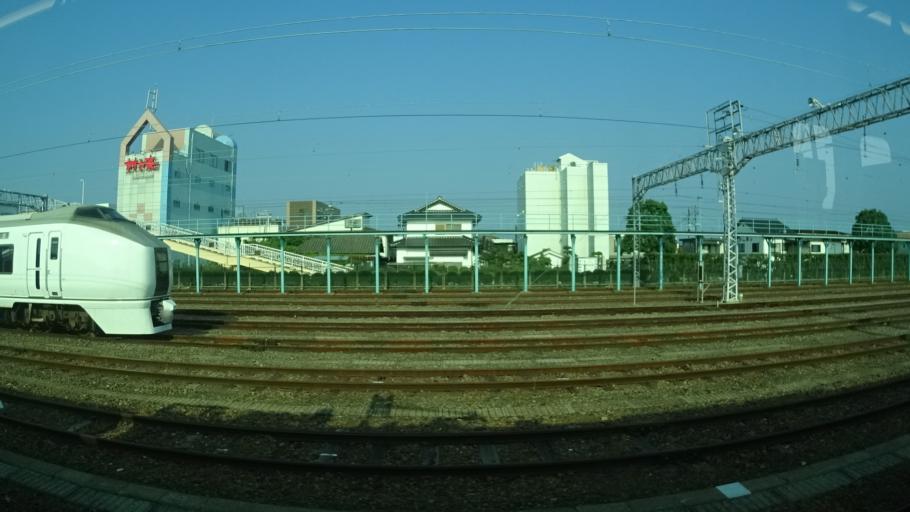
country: JP
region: Ibaraki
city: Takahagi
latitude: 36.7139
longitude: 140.7172
